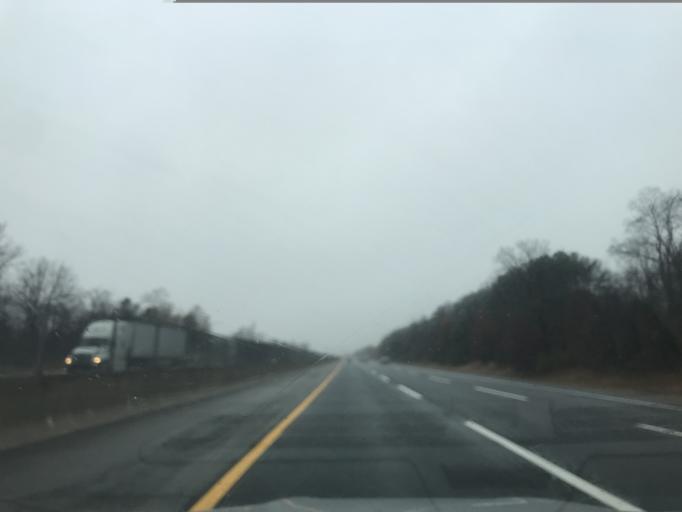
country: US
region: New Jersey
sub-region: Burlington County
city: Willingboro
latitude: 39.9844
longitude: -74.8841
